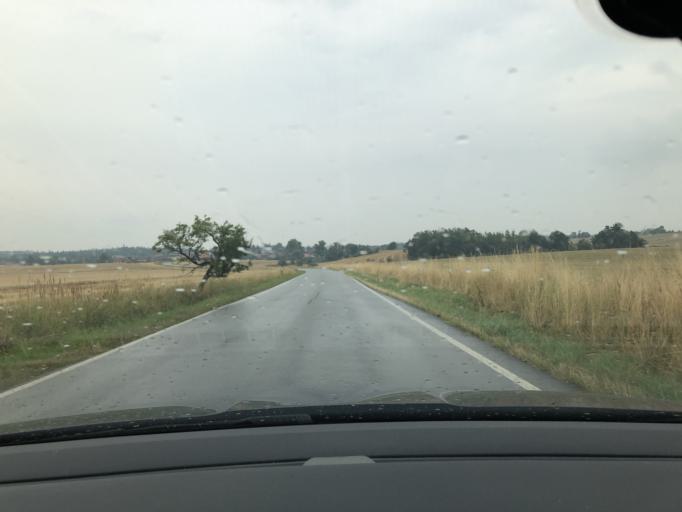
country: CZ
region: South Moravian
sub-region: Okres Znojmo
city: Jevisovice
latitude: 49.0291
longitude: 15.9655
